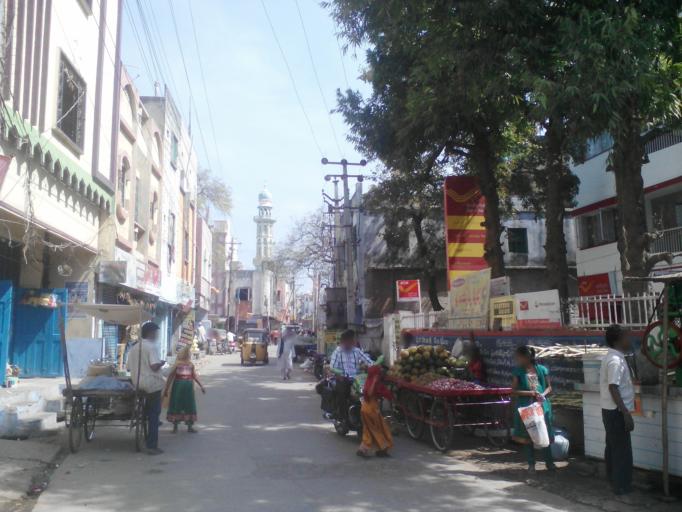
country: IN
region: Andhra Pradesh
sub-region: Kurnool
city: Nandyal
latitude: 15.4901
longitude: 78.4876
